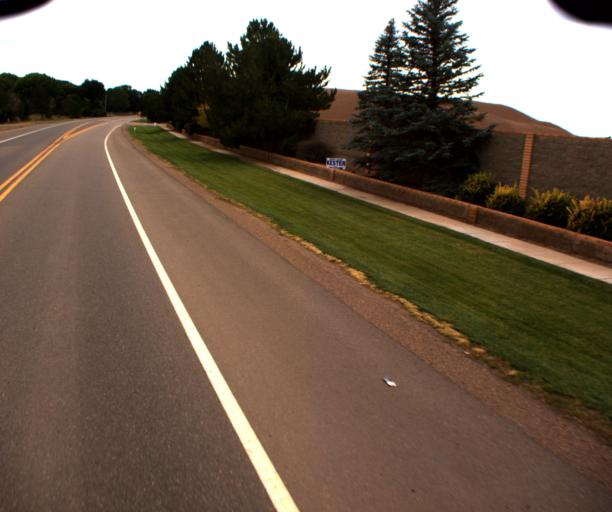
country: US
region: Arizona
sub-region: Navajo County
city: Snowflake
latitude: 34.5199
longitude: -110.0792
